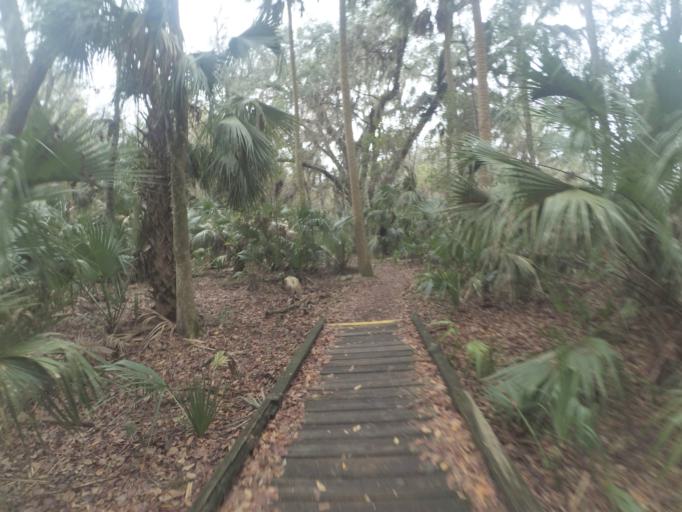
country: US
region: Florida
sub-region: Alachua County
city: Gainesville
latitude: 29.5492
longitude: -82.2925
